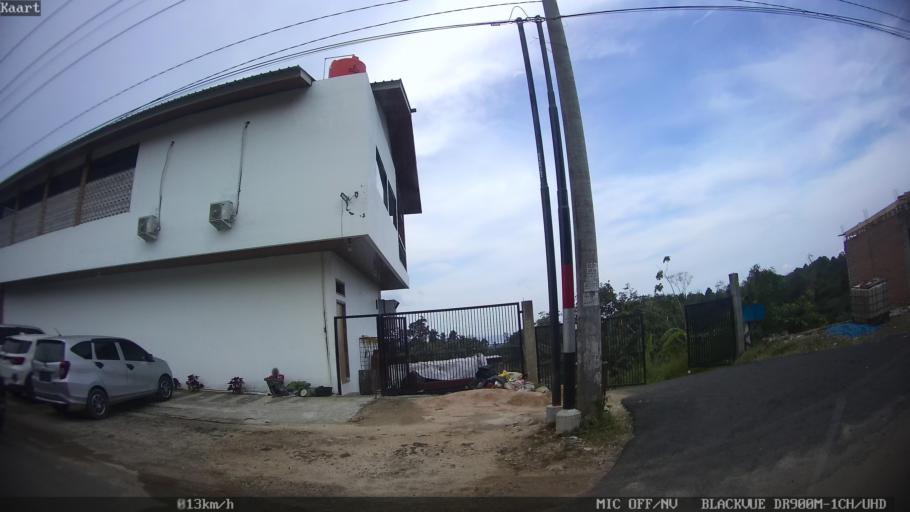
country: ID
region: Lampung
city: Bandarlampung
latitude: -5.4182
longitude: 105.1865
